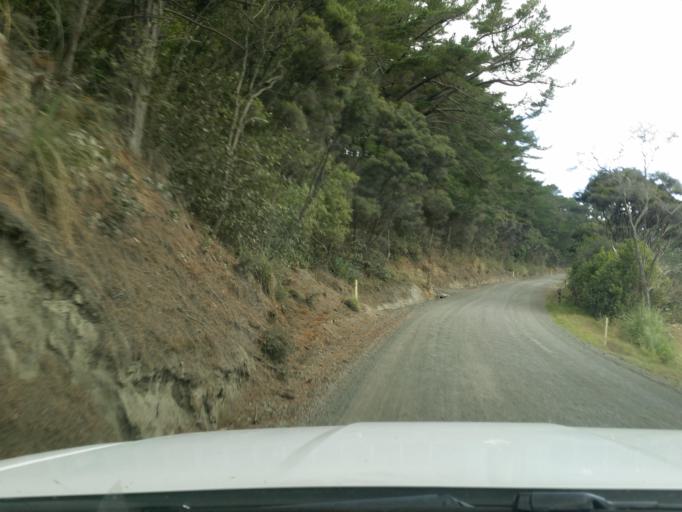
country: NZ
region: Auckland
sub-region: Auckland
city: Wellsford
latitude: -36.3098
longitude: 174.1248
